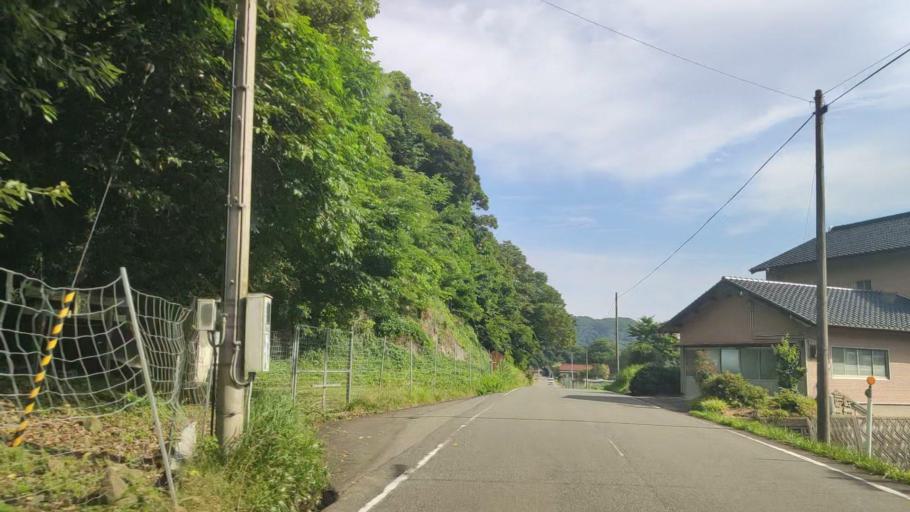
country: JP
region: Hyogo
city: Toyooka
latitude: 35.6355
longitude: 134.8366
